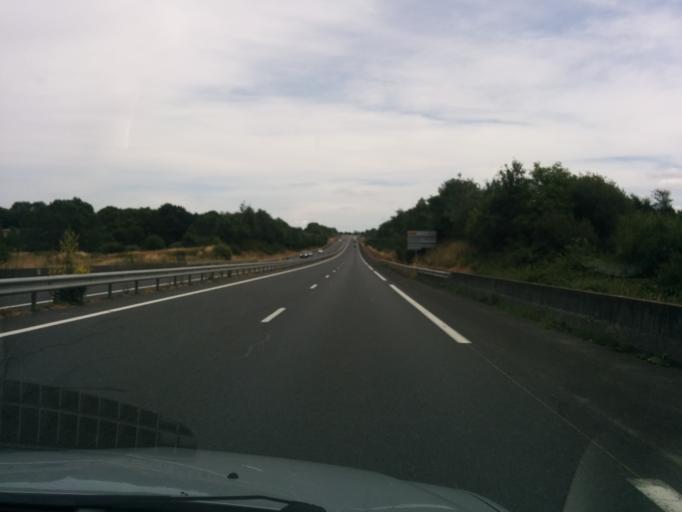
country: FR
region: Poitou-Charentes
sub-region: Departement des Deux-Sevres
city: Bressuire
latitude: 46.8572
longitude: -0.4932
